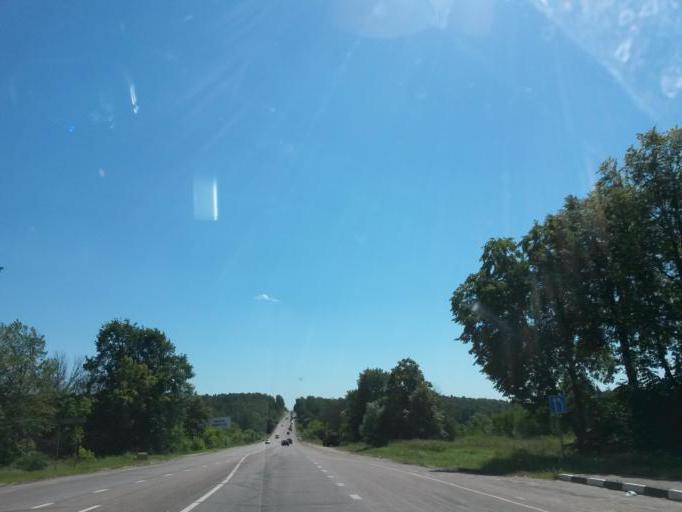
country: RU
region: Moskovskaya
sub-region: Chekhovskiy Rayon
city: Chekhov
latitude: 55.1136
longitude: 37.4477
